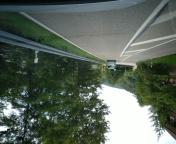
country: DE
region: Baden-Wuerttemberg
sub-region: Freiburg Region
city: Oppenau
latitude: 48.4371
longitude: 8.1721
